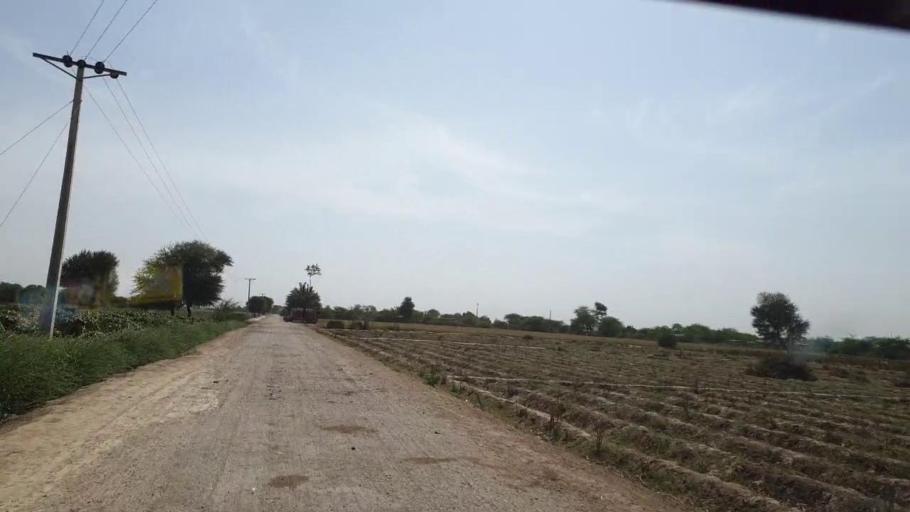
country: PK
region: Sindh
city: Kunri
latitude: 25.1144
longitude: 69.5682
